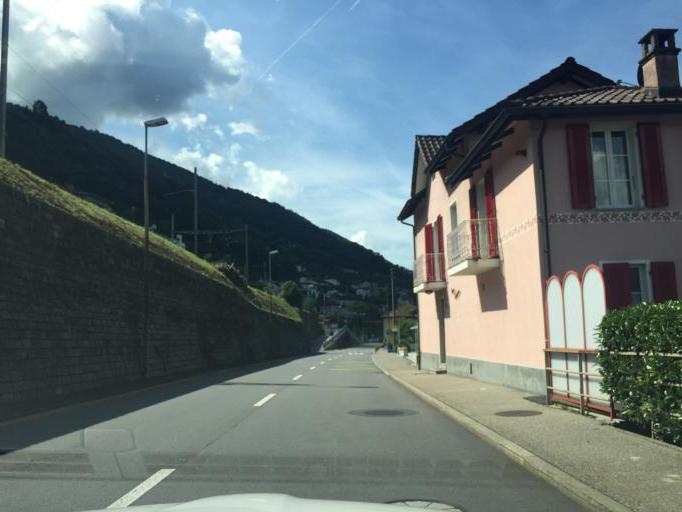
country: CH
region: Ticino
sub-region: Locarno District
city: Locarno
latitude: 46.1346
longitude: 8.8061
